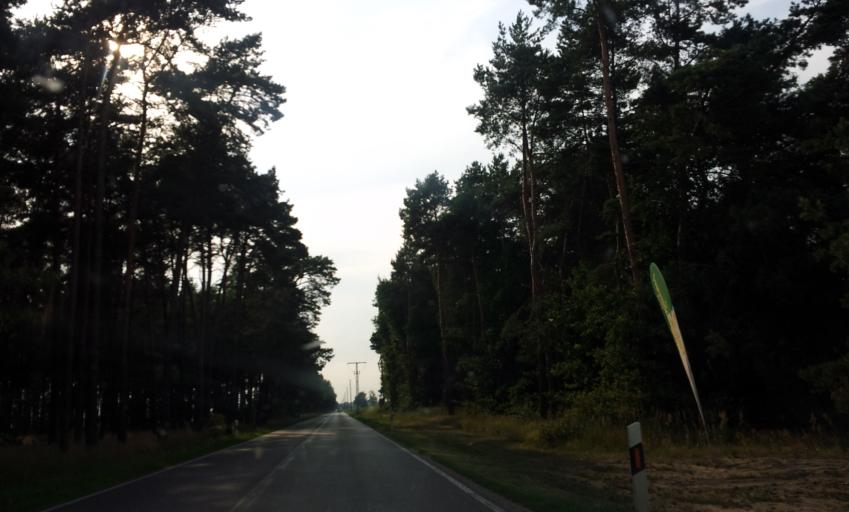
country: DE
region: Brandenburg
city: Juterbog
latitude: 52.1118
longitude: 13.0483
